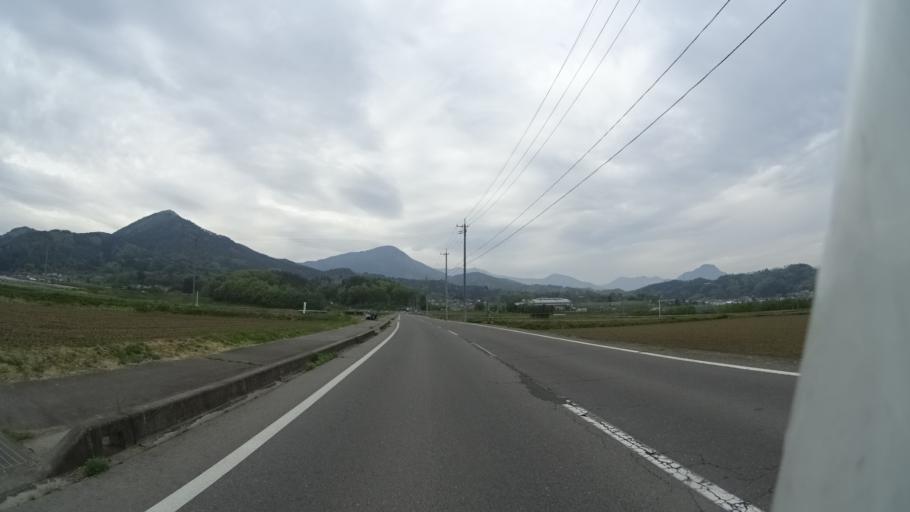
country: JP
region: Nagano
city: Kamimaruko
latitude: 36.3505
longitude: 138.1817
